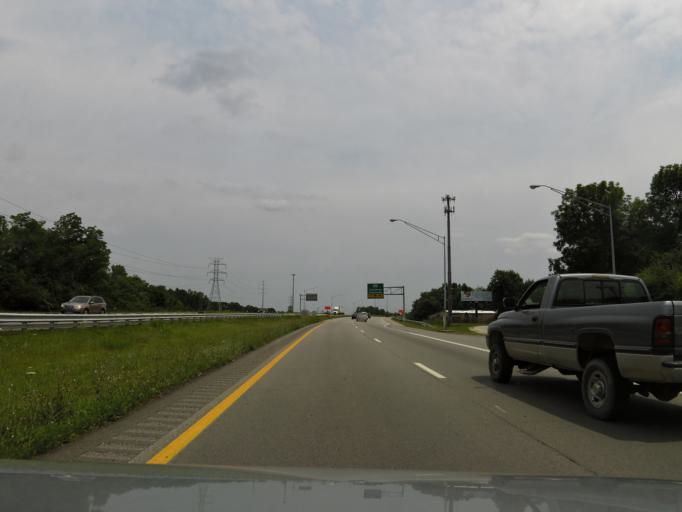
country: US
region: Ohio
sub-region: Montgomery County
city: Riverside
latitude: 39.7414
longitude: -84.1051
